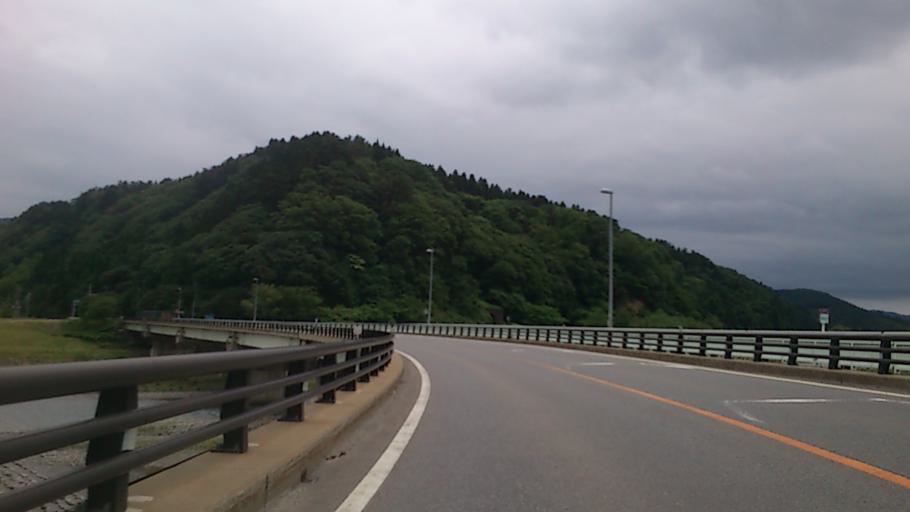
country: JP
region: Yamagata
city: Tsuruoka
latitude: 38.7835
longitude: 140.0260
